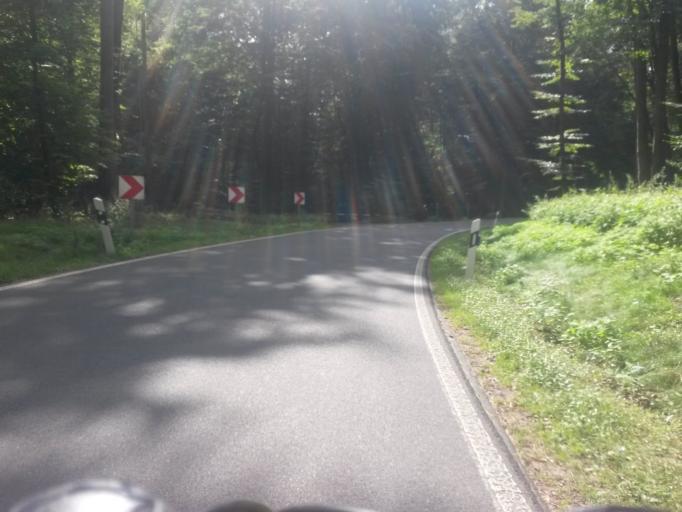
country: DE
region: Brandenburg
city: Angermunde
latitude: 53.0435
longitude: 13.9053
